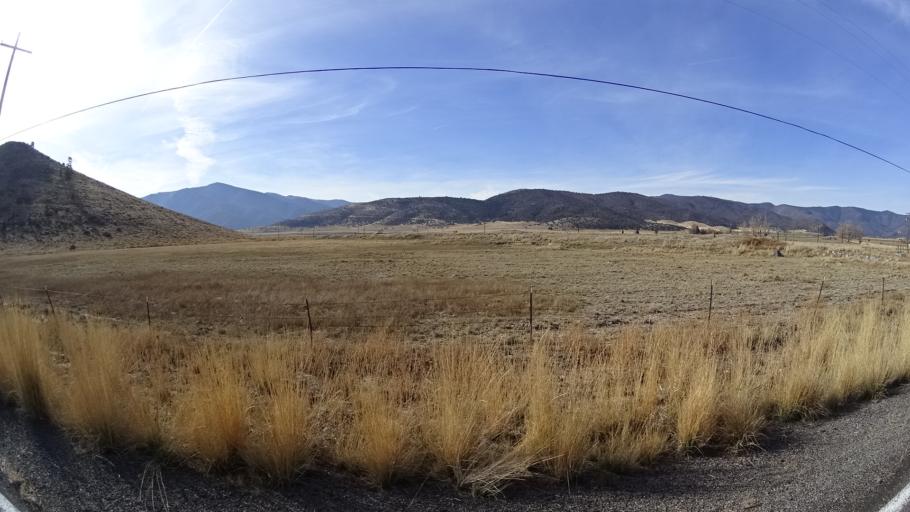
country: US
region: California
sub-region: Siskiyou County
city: Weed
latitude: 41.5377
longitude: -122.5228
